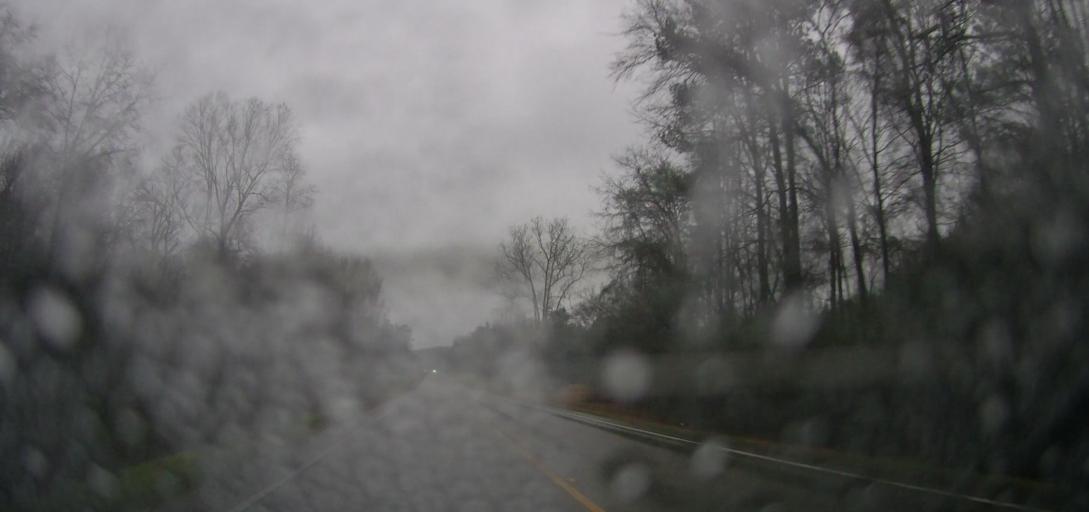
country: US
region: Alabama
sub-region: Autauga County
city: Prattville
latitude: 32.5093
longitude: -86.5873
